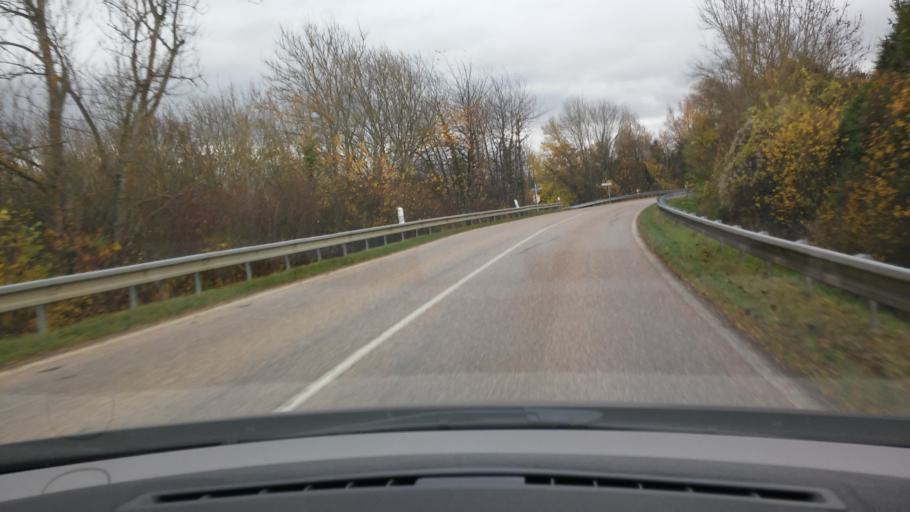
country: FR
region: Lorraine
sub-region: Departement de la Moselle
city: Saint-Julien-les-Metz
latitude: 49.1540
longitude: 6.2466
